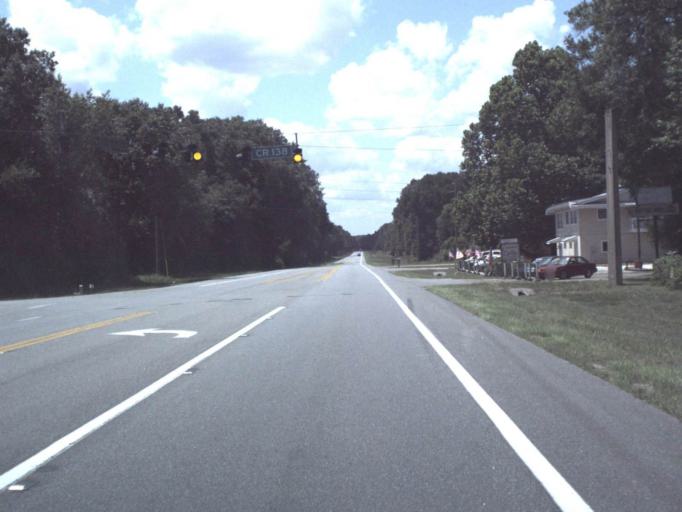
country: US
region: Florida
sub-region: Alachua County
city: High Springs
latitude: 29.8530
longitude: -82.6411
